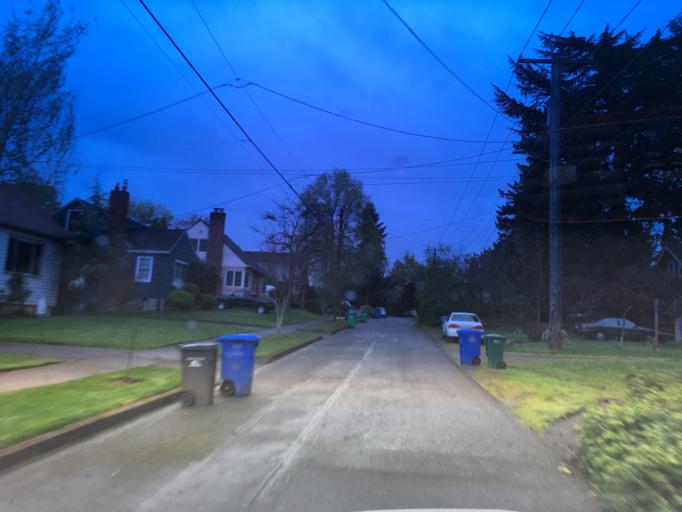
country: US
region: Oregon
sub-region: Multnomah County
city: Lents
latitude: 45.5535
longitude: -122.5993
